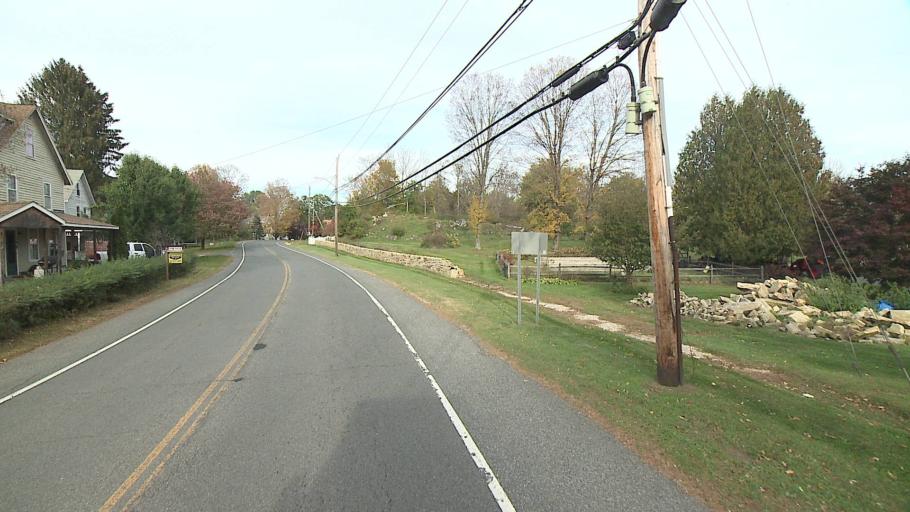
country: US
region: Connecticut
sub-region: Litchfield County
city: Canaan
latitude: 42.0244
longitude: -73.3398
